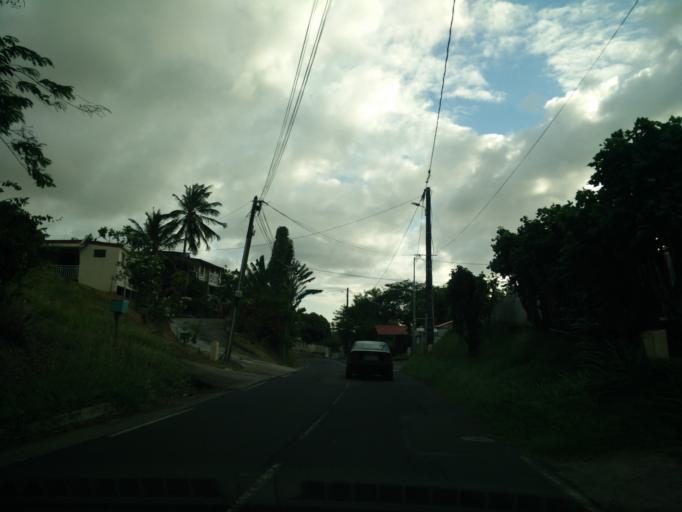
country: MQ
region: Martinique
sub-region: Martinique
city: Le Marin
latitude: 14.4641
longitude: -60.8544
